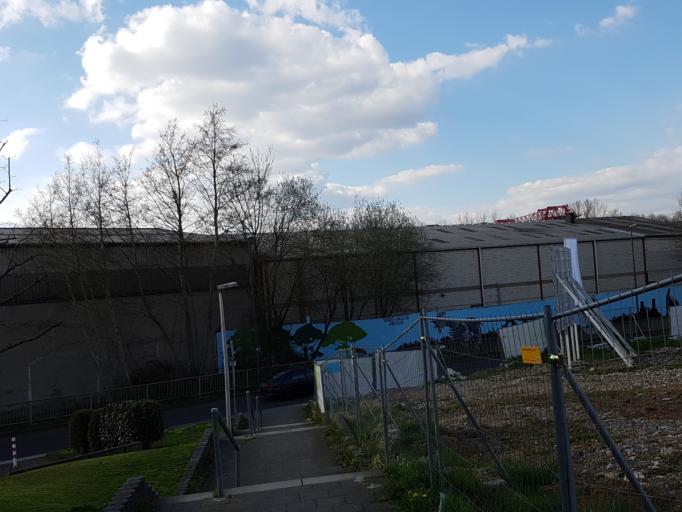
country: DE
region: North Rhine-Westphalia
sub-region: Regierungsbezirk Koln
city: Wurselen
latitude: 50.7806
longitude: 6.1429
